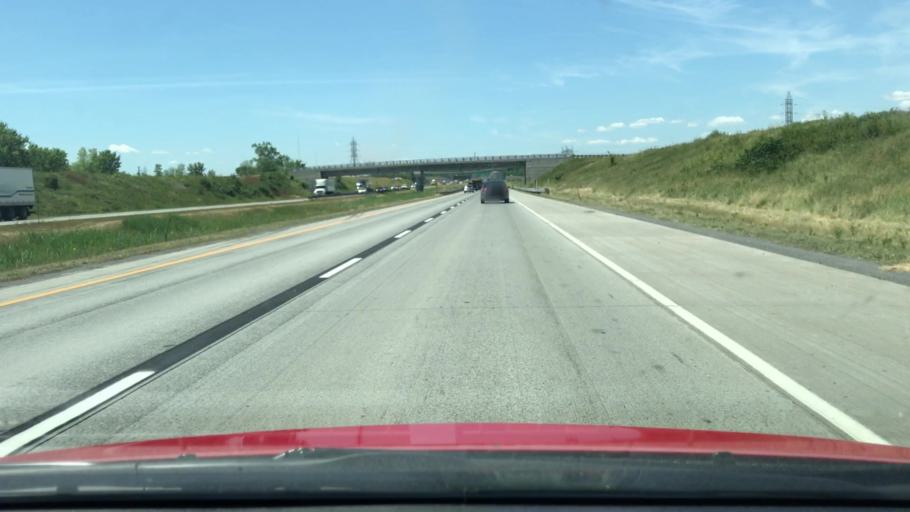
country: CA
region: Quebec
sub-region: Monteregie
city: Saint-Constant
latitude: 45.3663
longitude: -73.6057
